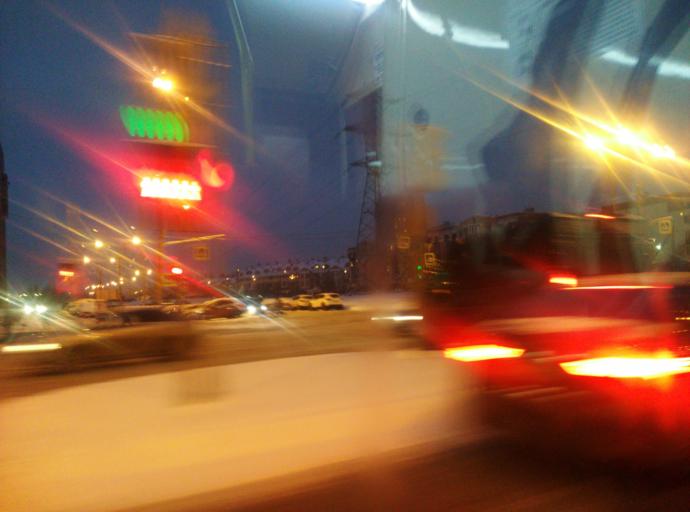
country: RU
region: St.-Petersburg
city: Komendantsky aerodrom
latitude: 60.0183
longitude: 30.2710
